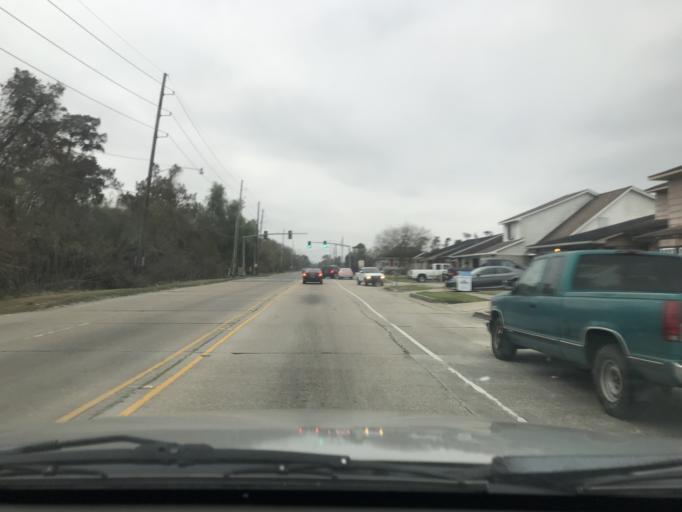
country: US
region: Louisiana
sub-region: Jefferson Parish
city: Woodmere
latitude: 29.8589
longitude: -90.0719
